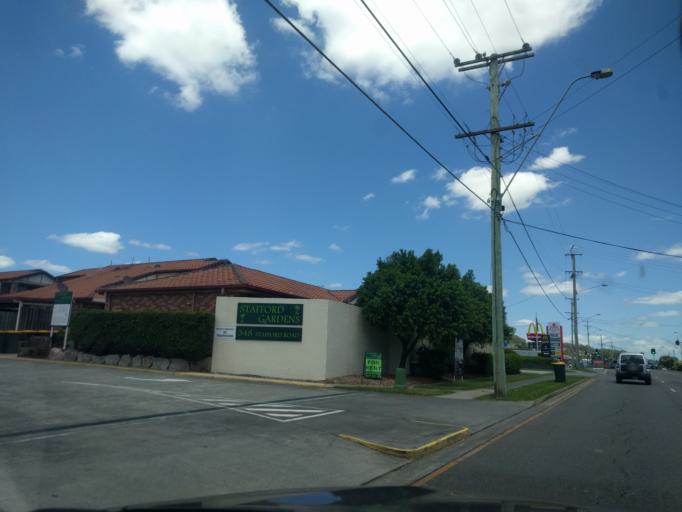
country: AU
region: Queensland
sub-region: Brisbane
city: Stafford
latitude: -27.4103
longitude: 153.0152
